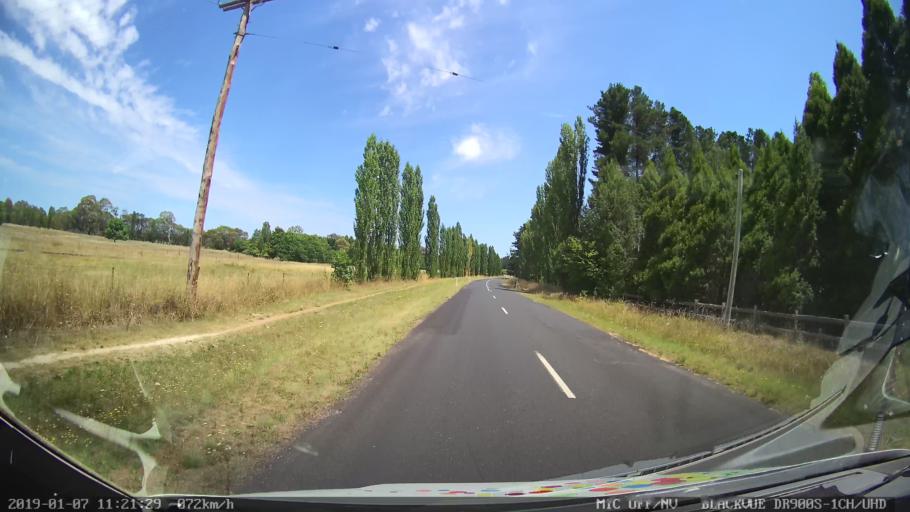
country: AU
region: New South Wales
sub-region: Armidale Dumaresq
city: Armidale
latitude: -30.4928
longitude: 151.6298
